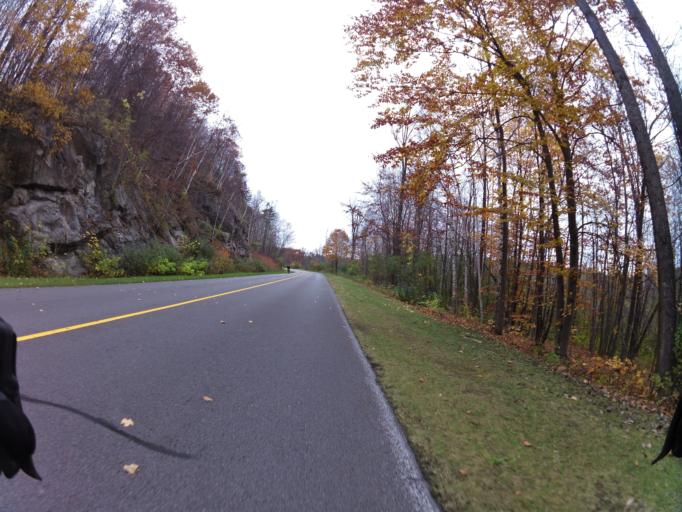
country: CA
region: Quebec
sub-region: Outaouais
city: Gatineau
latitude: 45.4618
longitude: -75.7907
